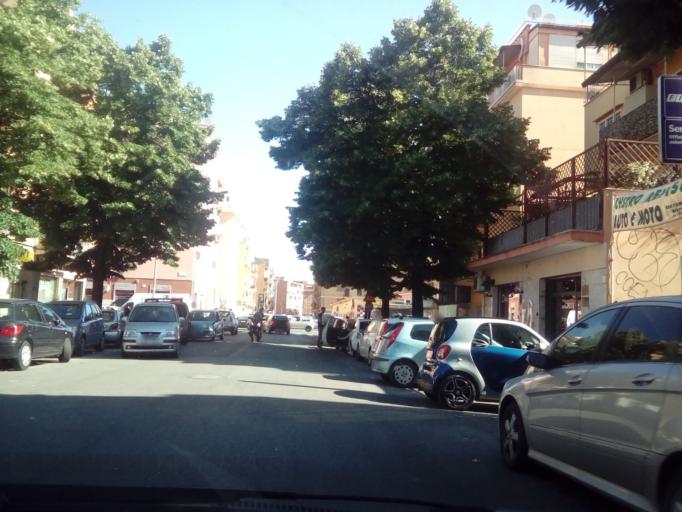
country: IT
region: Latium
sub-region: Citta metropolitana di Roma Capitale
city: Rome
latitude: 41.8886
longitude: 12.5673
